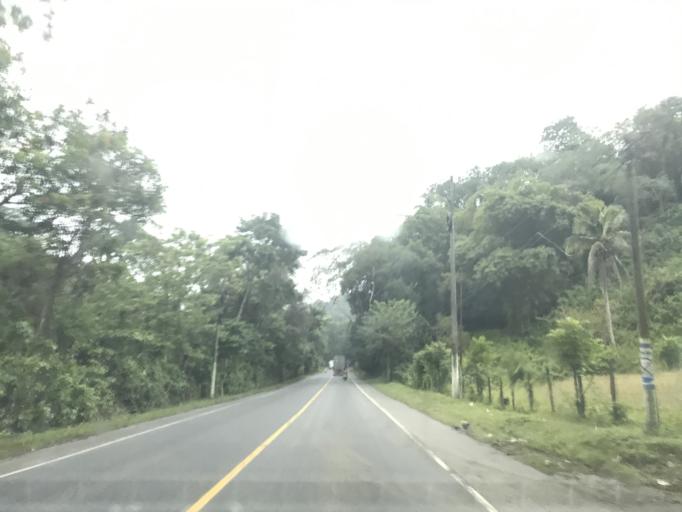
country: GT
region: Izabal
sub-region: Municipio de Puerto Barrios
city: Puerto Barrios
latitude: 15.6663
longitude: -88.5598
